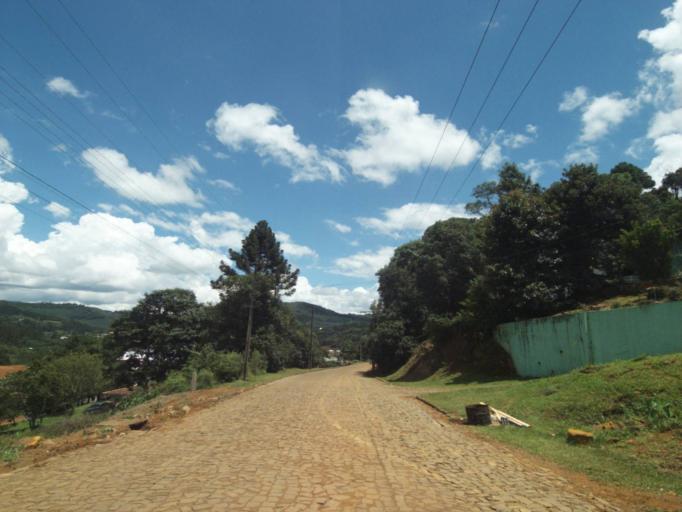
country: BR
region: Parana
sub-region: Uniao Da Vitoria
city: Uniao da Vitoria
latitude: -26.1633
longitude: -51.5563
